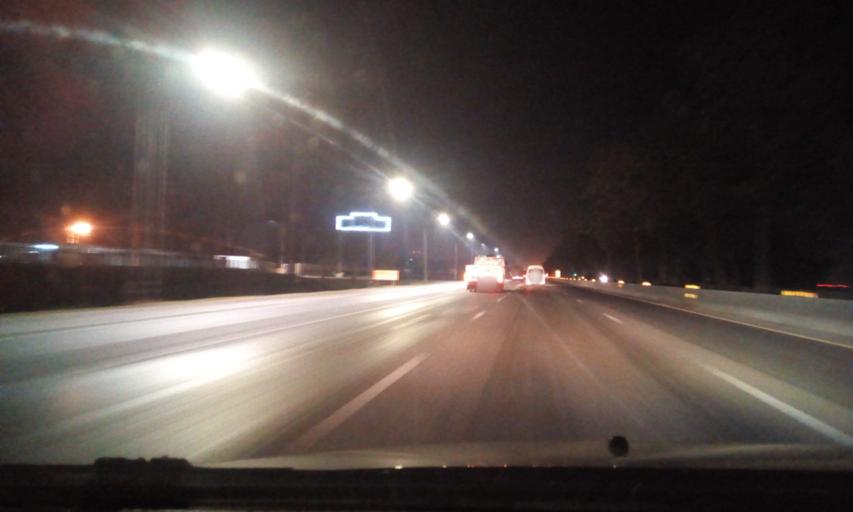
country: TH
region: Sing Buri
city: Phrom Buri
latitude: 14.7392
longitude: 100.4545
